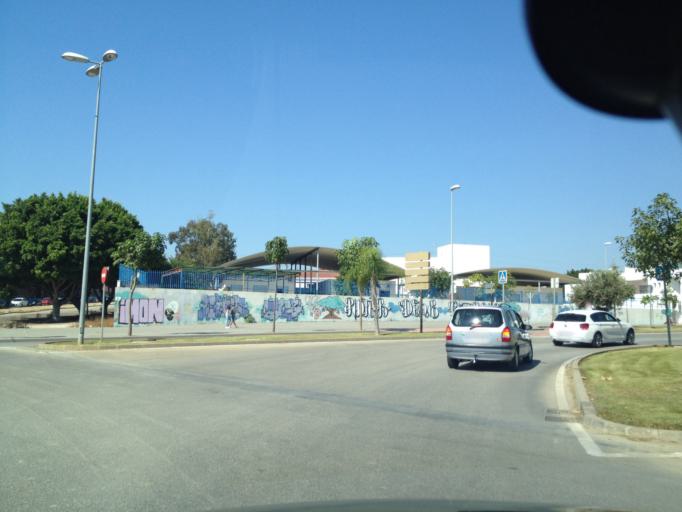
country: ES
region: Andalusia
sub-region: Provincia de Malaga
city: Malaga
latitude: 36.7205
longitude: -4.4686
